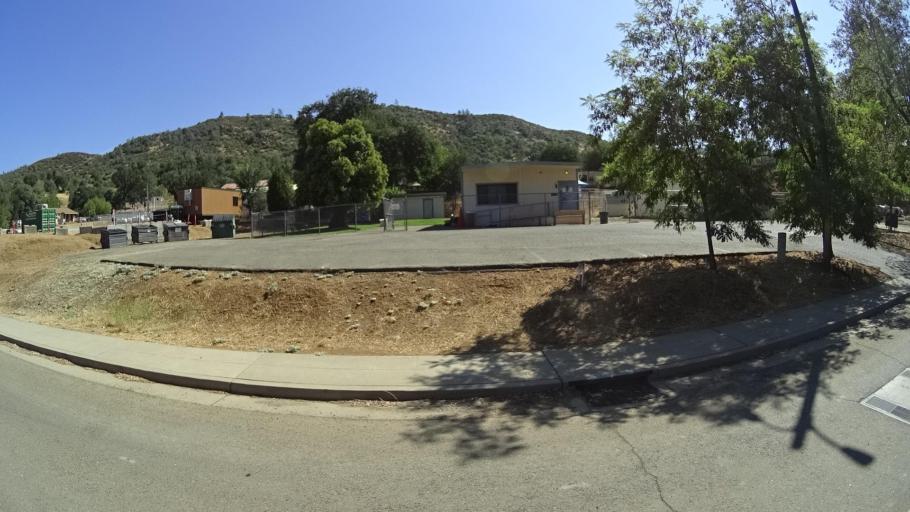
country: US
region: California
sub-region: Mariposa County
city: Mariposa
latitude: 37.4878
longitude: -119.9654
